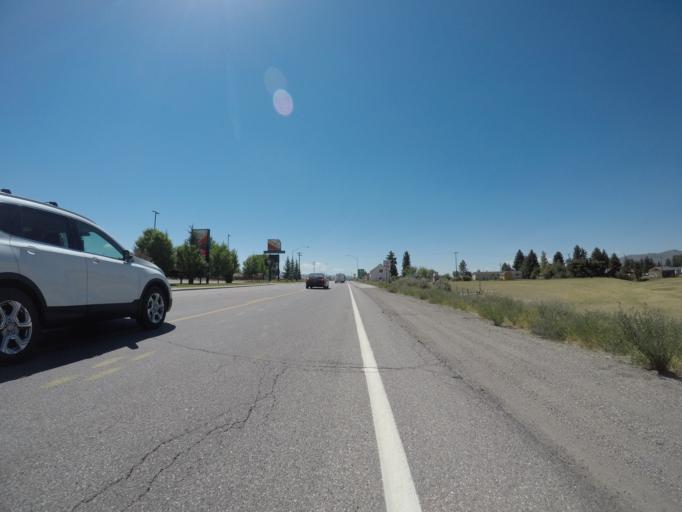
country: US
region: Idaho
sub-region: Bear Lake County
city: Montpelier
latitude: 42.0871
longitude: -110.9490
